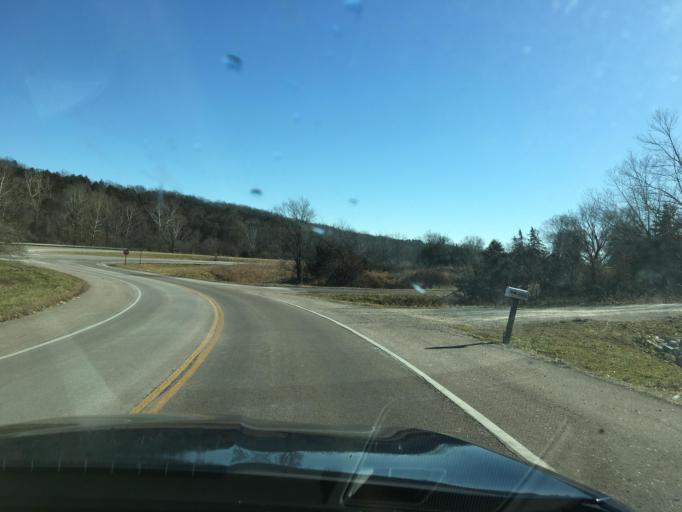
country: US
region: Missouri
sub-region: Jefferson County
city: De Soto
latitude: 38.1519
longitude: -90.5417
